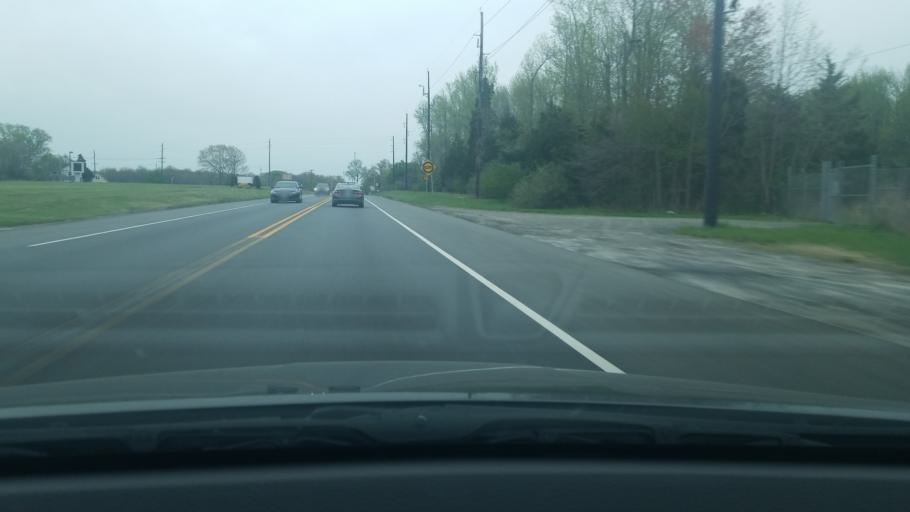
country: US
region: New Jersey
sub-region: Burlington County
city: Leisuretowne
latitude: 39.8875
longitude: -74.7456
